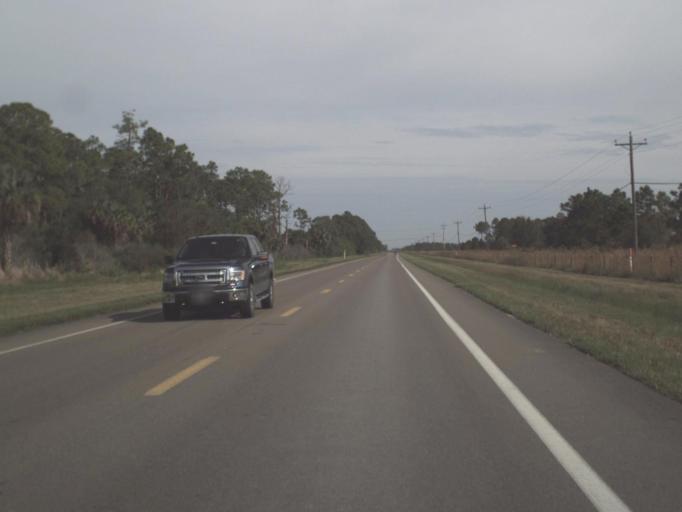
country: US
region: Florida
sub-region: Lee County
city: Fort Myers Shores
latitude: 26.8188
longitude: -81.7601
